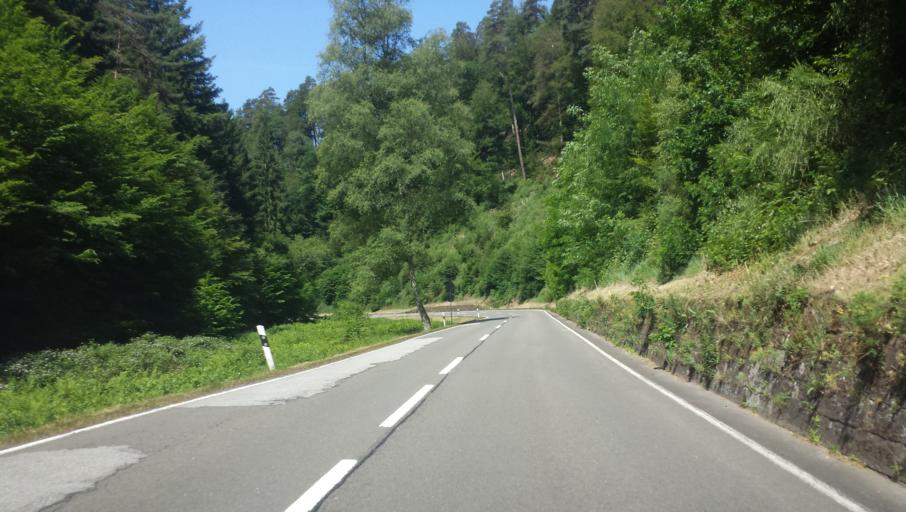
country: DE
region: Rheinland-Pfalz
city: Elmstein
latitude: 49.3596
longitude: 7.9159
